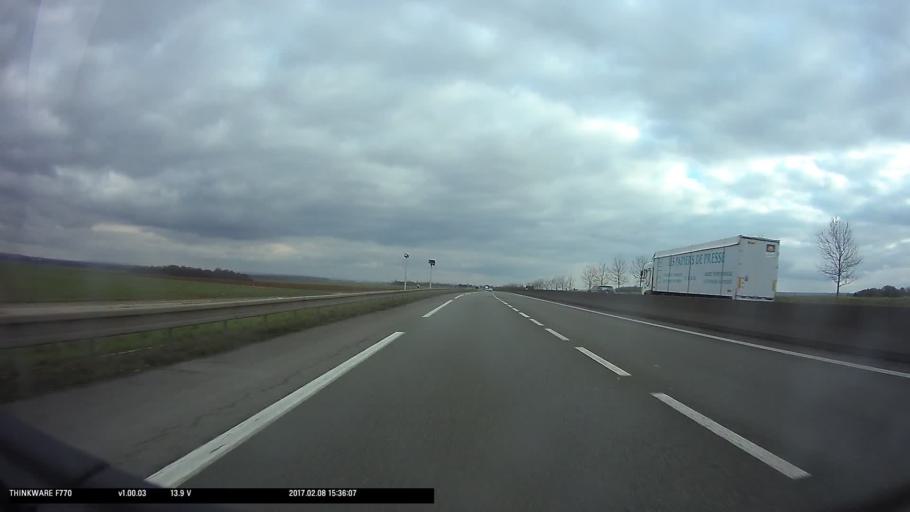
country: FR
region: Ile-de-France
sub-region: Departement du Val-d'Oise
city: Vigny
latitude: 49.0803
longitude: 1.9377
